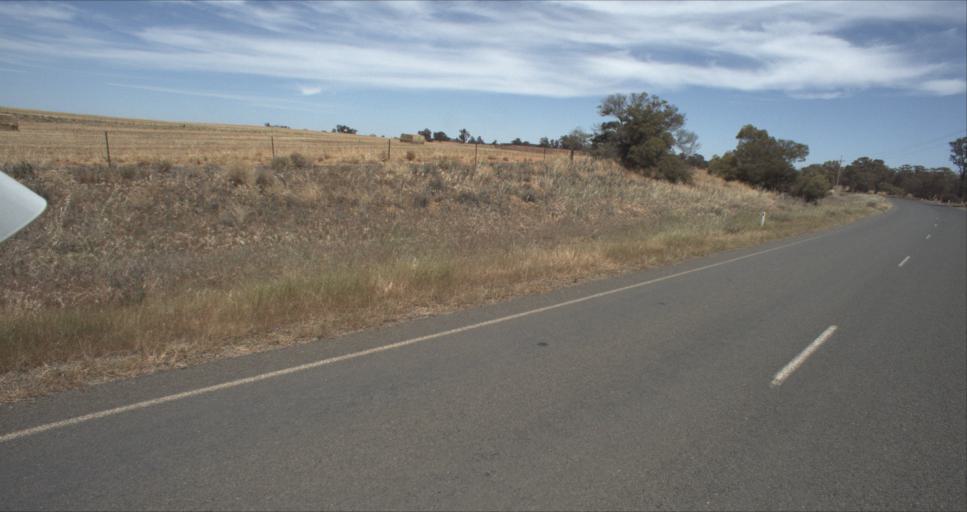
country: AU
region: New South Wales
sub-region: Leeton
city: Leeton
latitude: -34.6526
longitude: 146.4630
